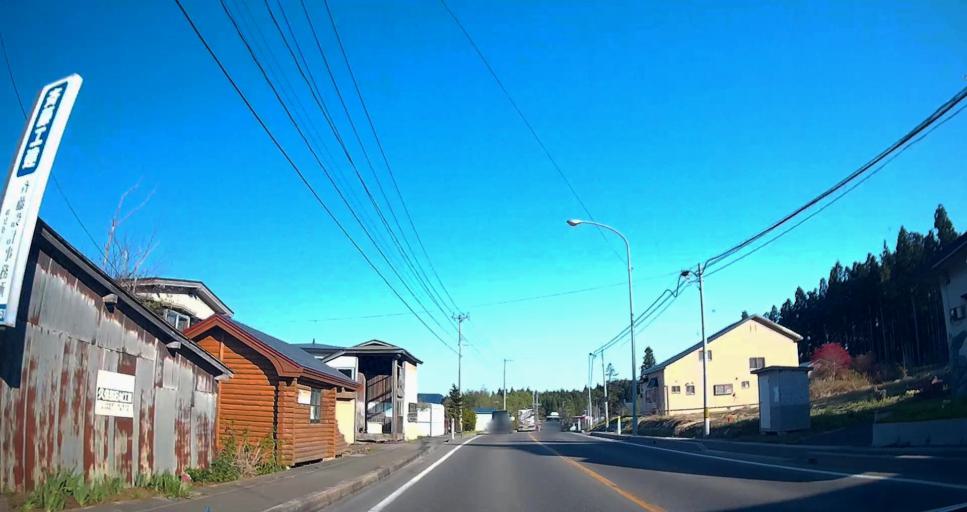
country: JP
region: Aomori
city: Mutsu
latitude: 41.3287
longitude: 141.2162
